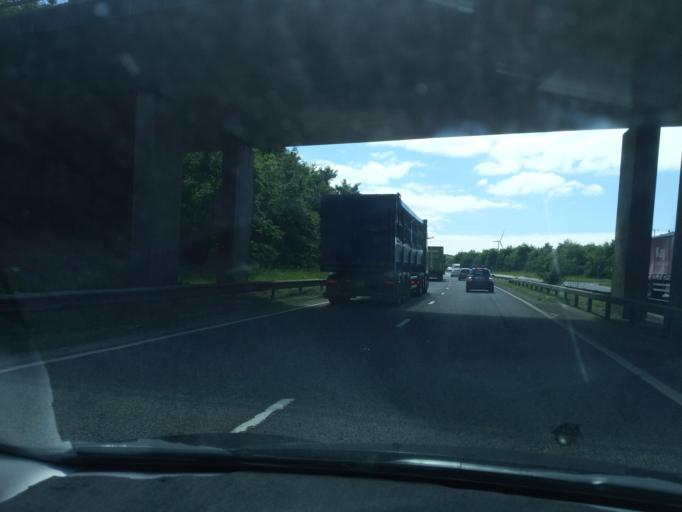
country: GB
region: England
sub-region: Cornwall
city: Probus
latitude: 50.3537
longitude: -5.0069
